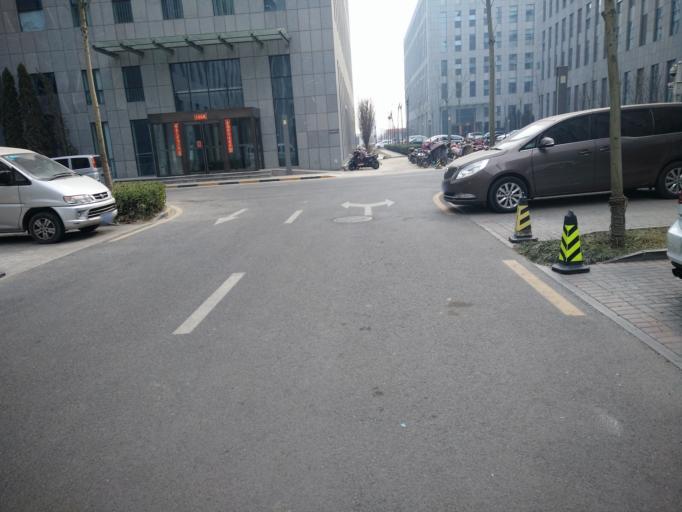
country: CN
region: Beijing
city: Jiugong
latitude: 39.7612
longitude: 116.5089
